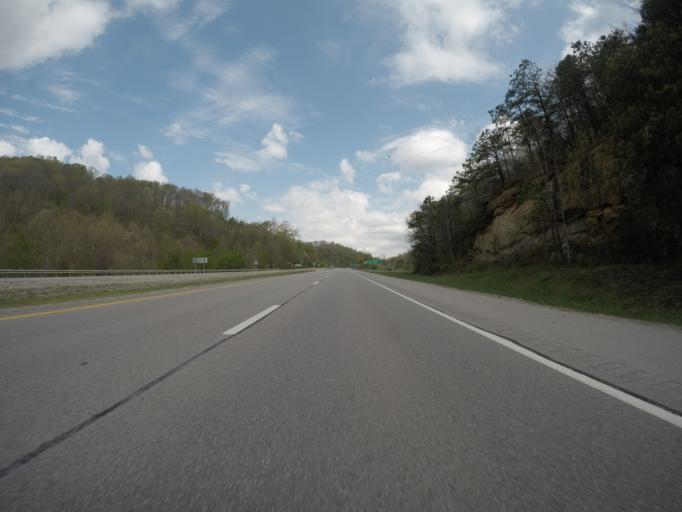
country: US
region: West Virginia
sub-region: Kanawha County
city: Alum Creek
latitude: 38.2257
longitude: -81.8365
